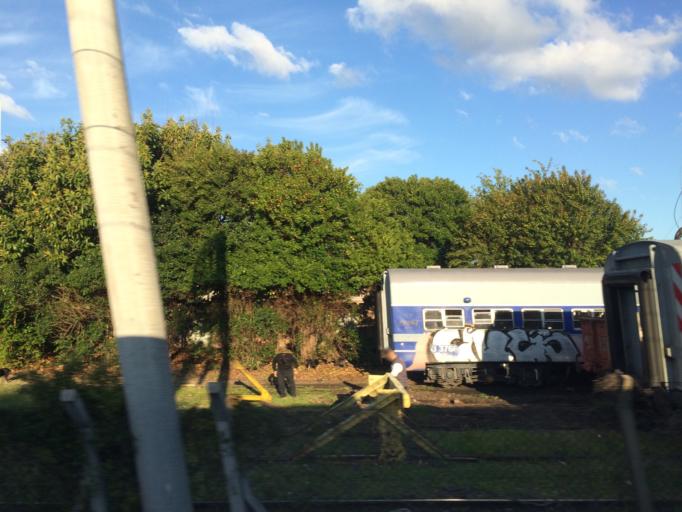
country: AR
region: Buenos Aires
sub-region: Partido de Lanus
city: Lanus
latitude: -34.7233
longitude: -58.3932
